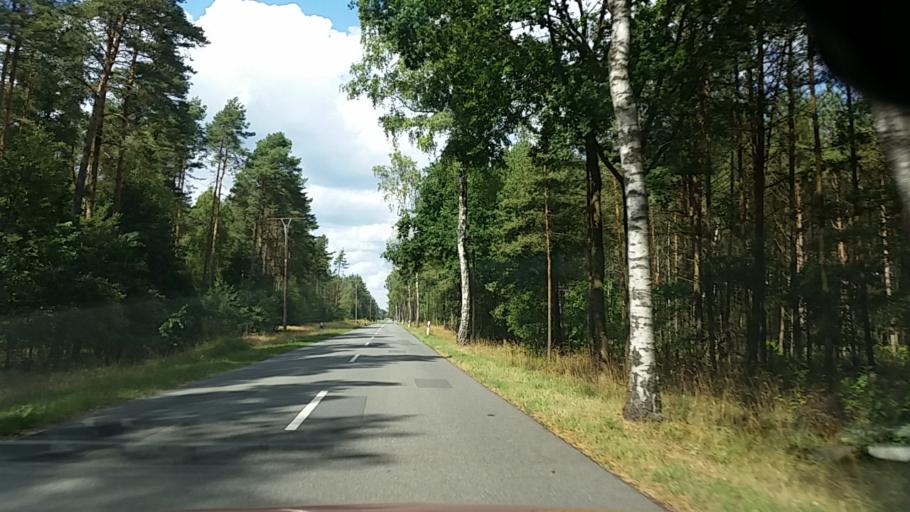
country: DE
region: Lower Saxony
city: Dedelstorf
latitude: 52.7133
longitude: 10.5290
